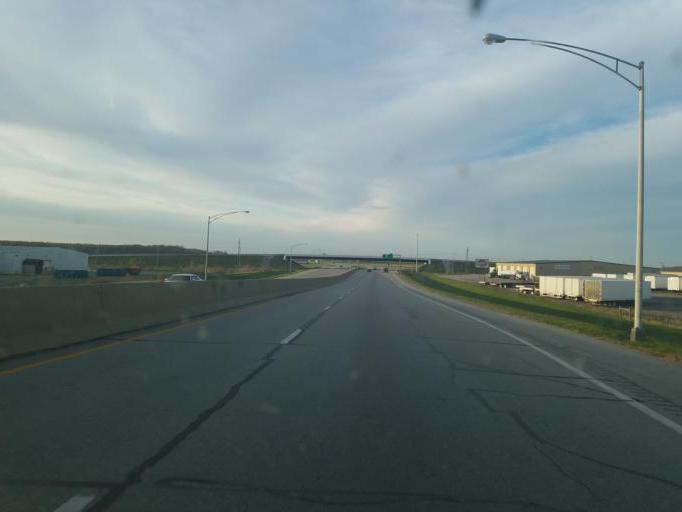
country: US
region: Ohio
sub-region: Wood County
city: Millbury
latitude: 41.5561
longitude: -83.4607
